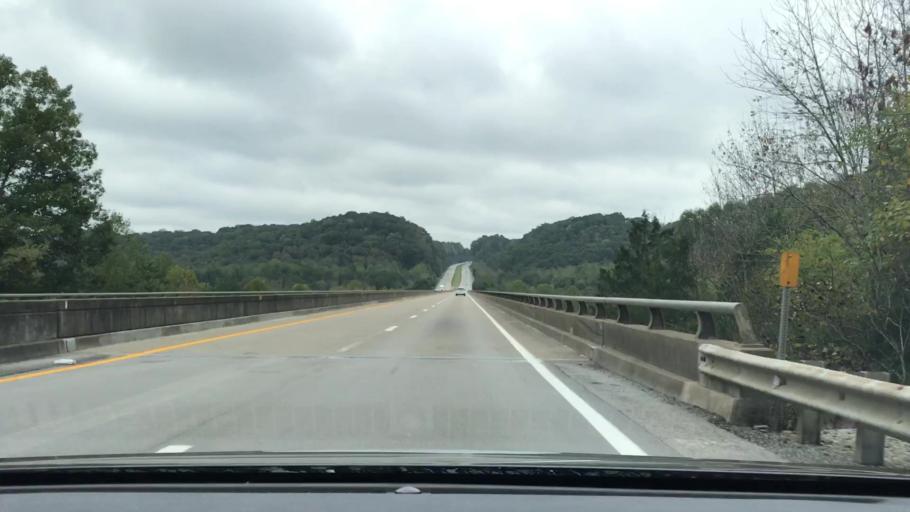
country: US
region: Kentucky
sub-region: Pulaski County
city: Somerset
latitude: 37.0980
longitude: -84.6884
